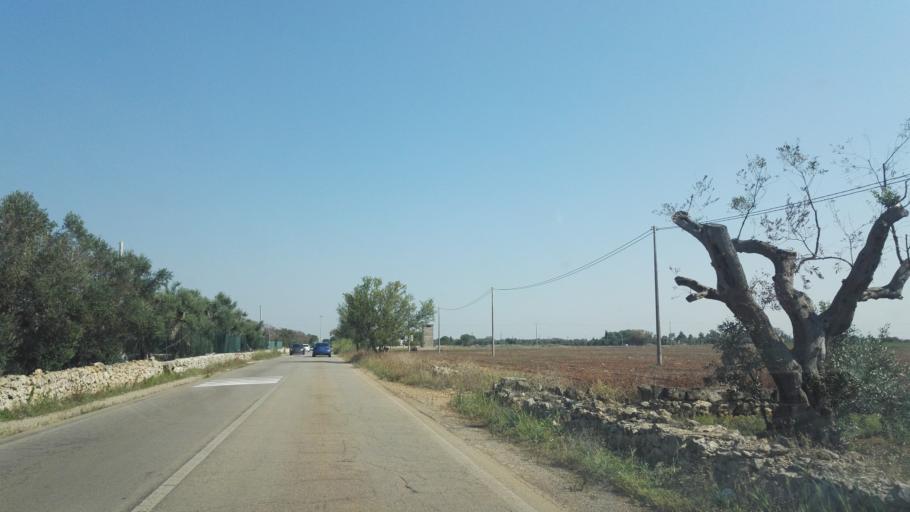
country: IT
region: Apulia
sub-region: Provincia di Lecce
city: Nardo
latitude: 40.1227
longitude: 18.0198
